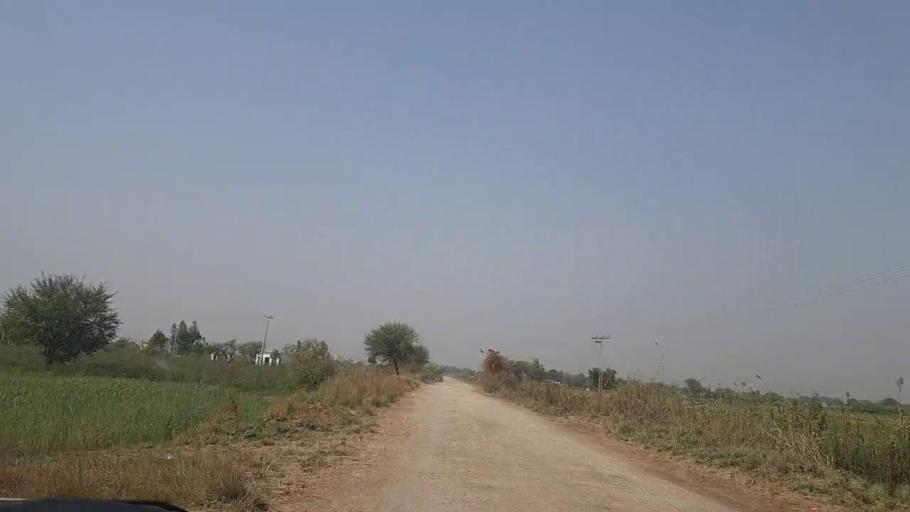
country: PK
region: Sindh
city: Pithoro
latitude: 25.5756
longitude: 69.2027
